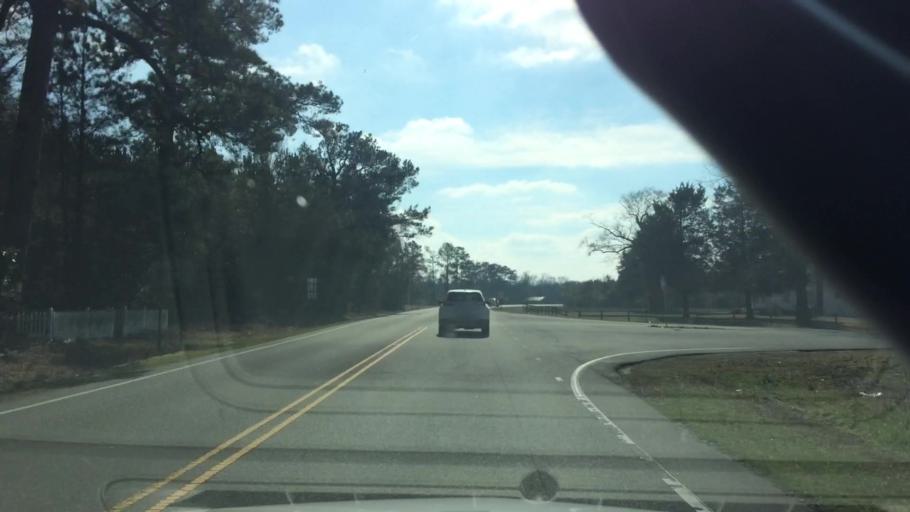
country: US
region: North Carolina
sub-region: Duplin County
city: Beulaville
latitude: 34.8241
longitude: -77.8390
